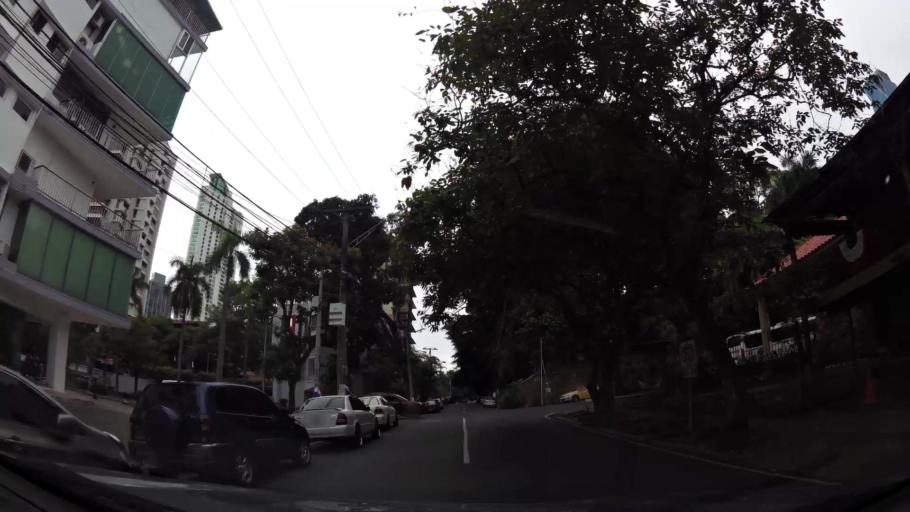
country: PA
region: Panama
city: Panama
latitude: 8.9780
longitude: -79.5270
